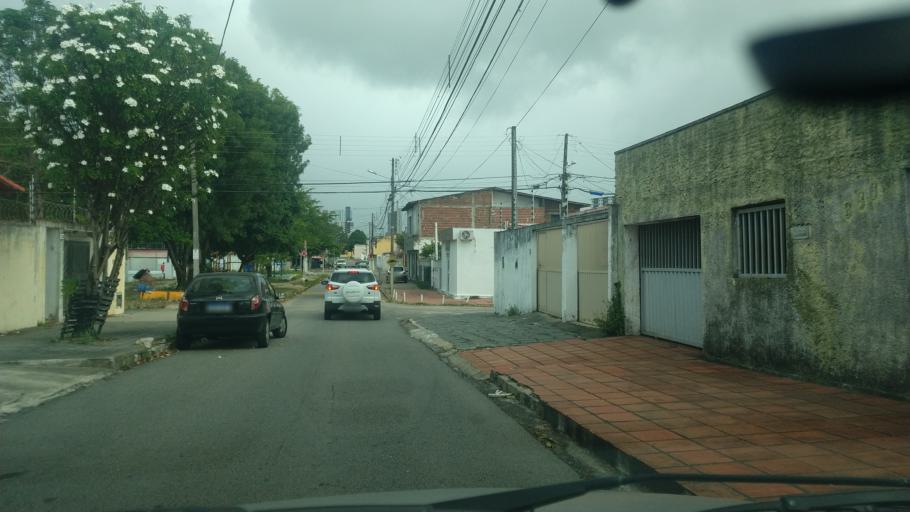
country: BR
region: Rio Grande do Norte
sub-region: Natal
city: Natal
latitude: -5.8292
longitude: -35.2090
